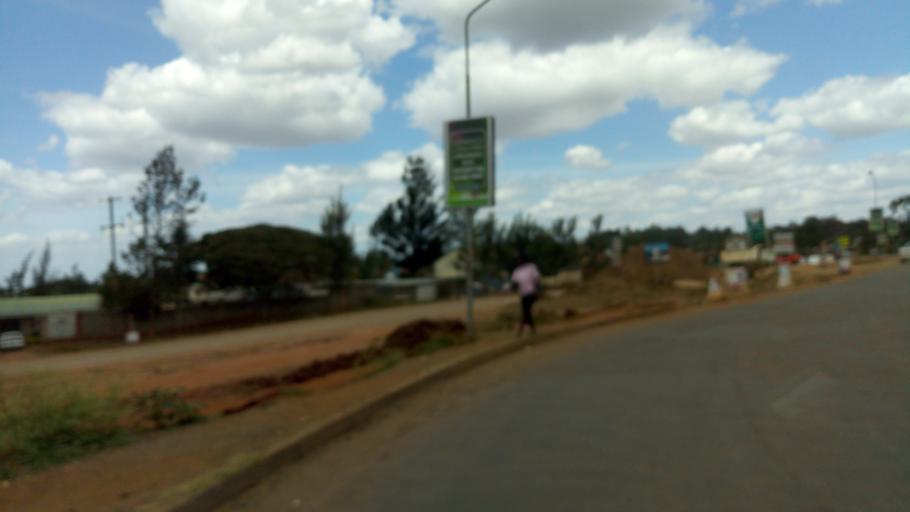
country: KE
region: Nairobi Area
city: Nairobi
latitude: -1.3264
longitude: 36.7803
